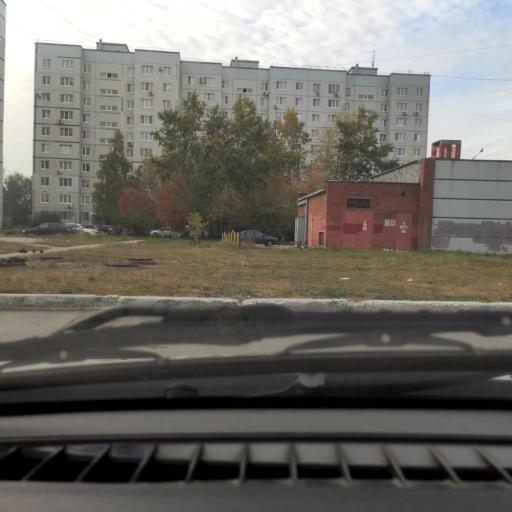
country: RU
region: Samara
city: Tol'yatti
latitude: 53.5411
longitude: 49.3997
